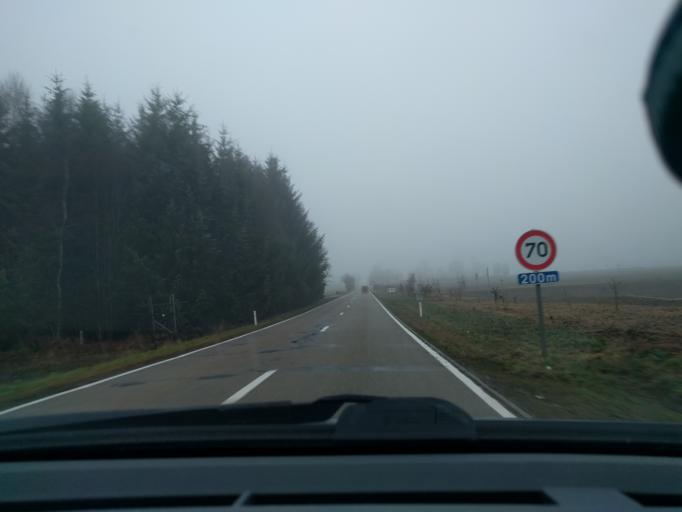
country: BE
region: Wallonia
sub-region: Province du Luxembourg
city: Gouvy
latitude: 50.2018
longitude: 5.9219
